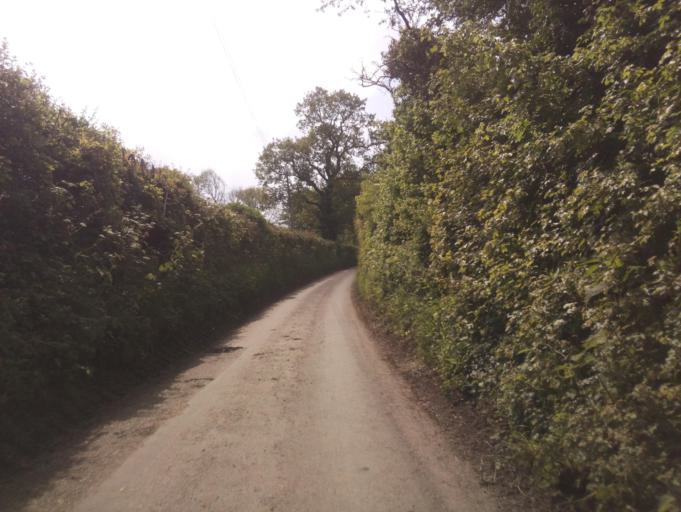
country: GB
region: England
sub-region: South Gloucestershire
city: Horton
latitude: 51.5421
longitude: -2.3571
